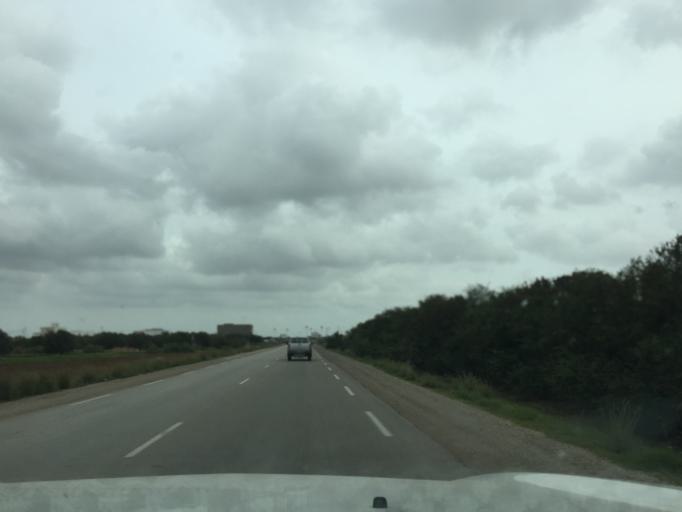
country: TN
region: Al Munastir
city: Manzil Kamil
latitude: 35.6204
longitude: 10.6808
